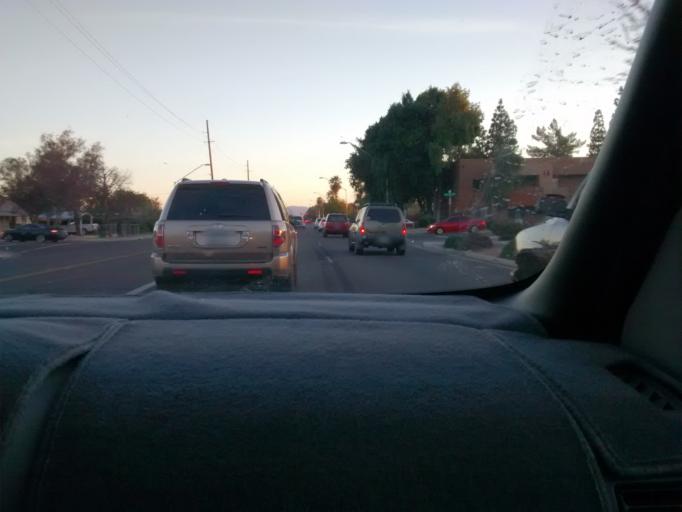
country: US
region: Arizona
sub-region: Maricopa County
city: Glendale
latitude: 33.5351
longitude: -112.2030
